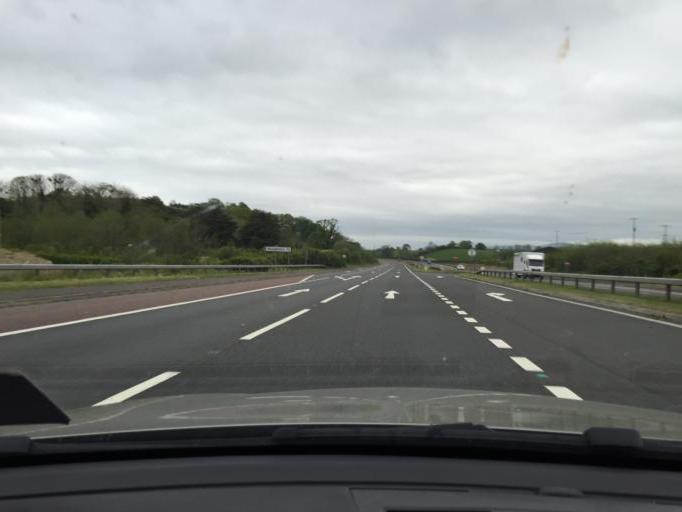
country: GB
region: Northern Ireland
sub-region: Newry and Mourne District
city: Newry
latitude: 54.2505
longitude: -6.3207
